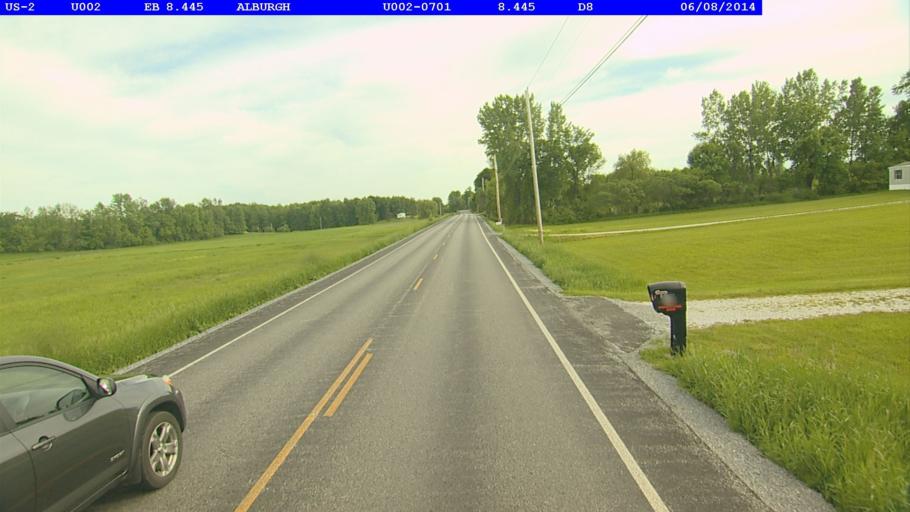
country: US
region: New York
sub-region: Clinton County
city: Rouses Point
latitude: 44.9290
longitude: -73.2745
